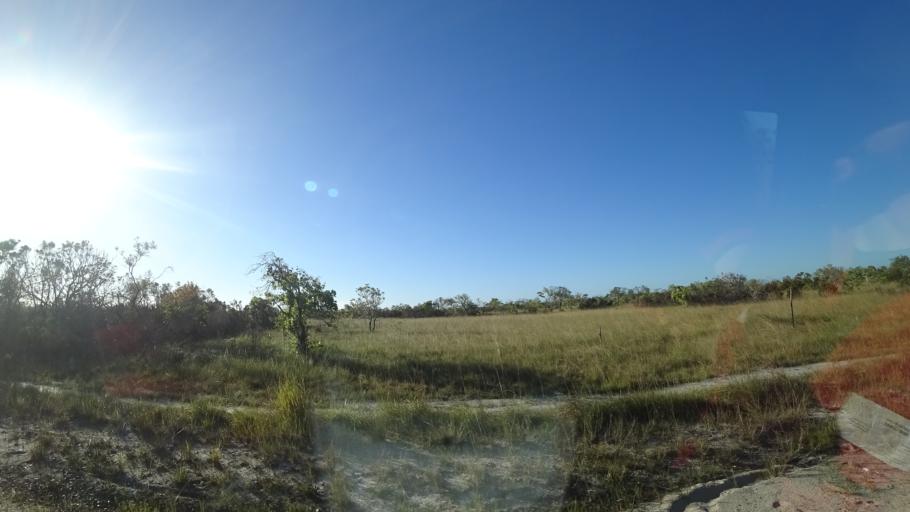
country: MZ
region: Sofala
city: Beira
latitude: -19.5765
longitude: 35.1949
